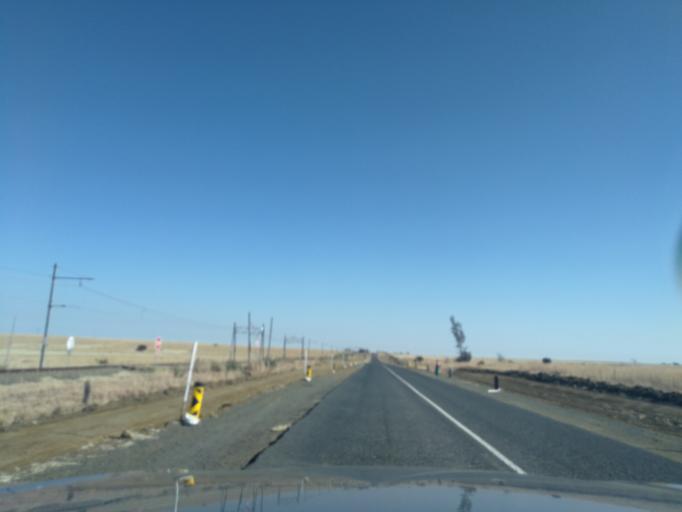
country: ZA
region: Orange Free State
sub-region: Fezile Dabi District Municipality
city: Kroonstad
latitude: -27.8966
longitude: 27.4991
